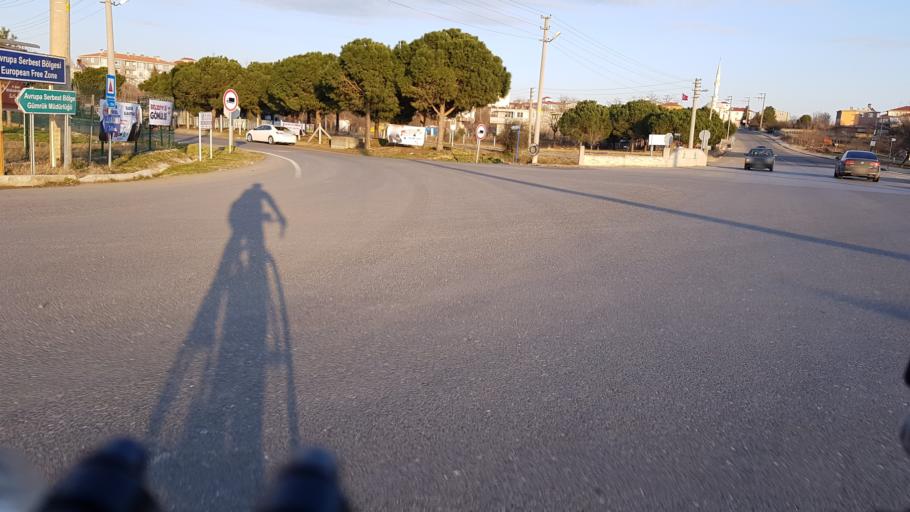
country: TR
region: Tekirdag
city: Velimese
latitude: 41.2497
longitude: 27.8730
